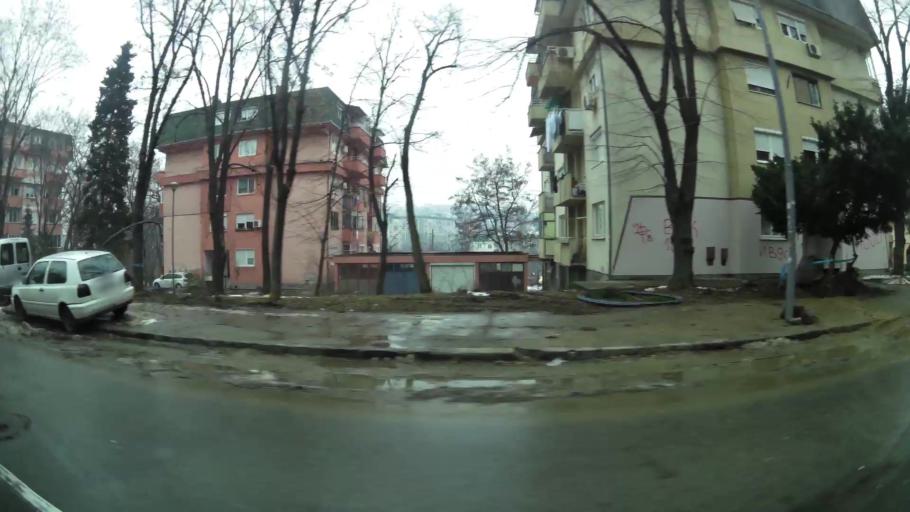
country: RS
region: Central Serbia
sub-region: Belgrade
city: Vozdovac
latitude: 44.7767
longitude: 20.4846
